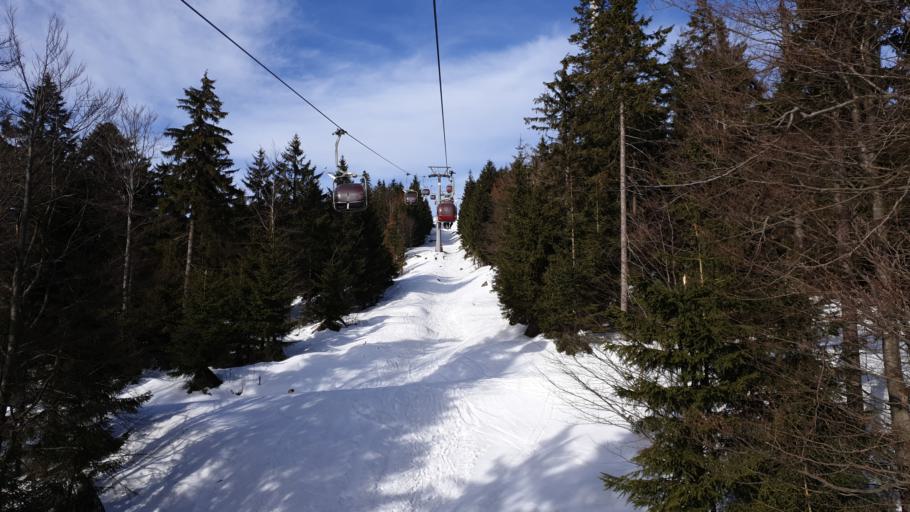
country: DE
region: Bavaria
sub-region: Upper Franconia
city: Bischofsgrun
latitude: 50.0271
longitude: 11.8077
